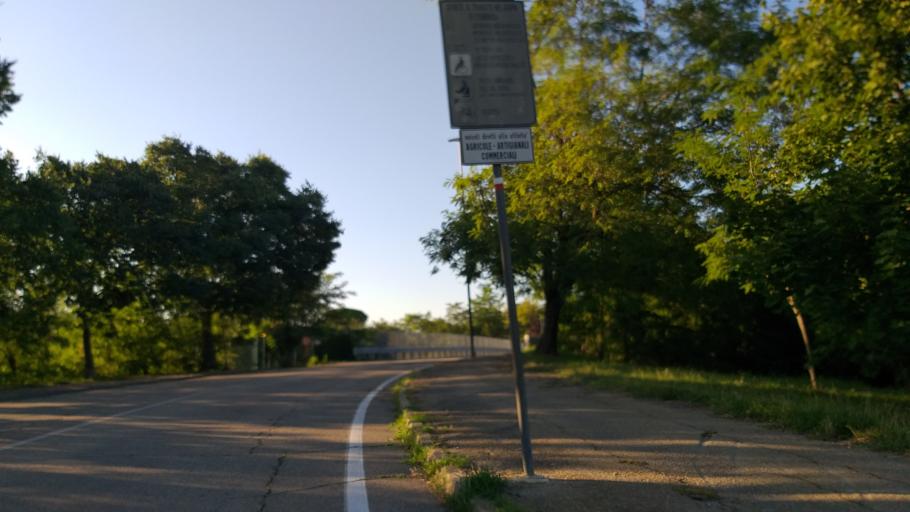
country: IT
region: Piedmont
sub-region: Provincia di Asti
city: Asti
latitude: 44.9172
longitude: 8.2021
